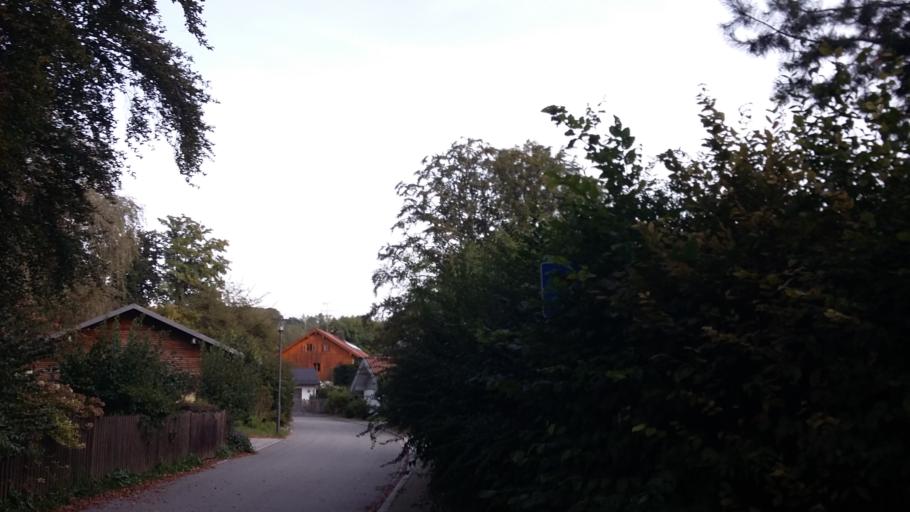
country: DE
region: Bavaria
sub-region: Upper Bavaria
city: Bernried
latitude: 47.8719
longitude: 11.3327
